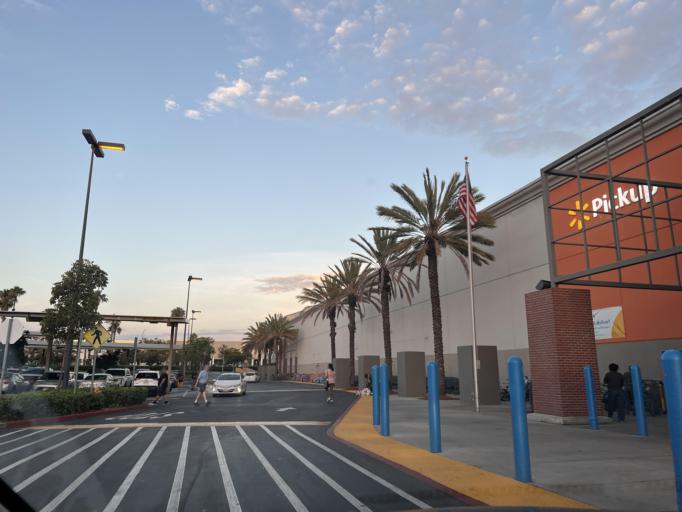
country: US
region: California
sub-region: San Diego County
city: La Jolla
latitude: 32.8301
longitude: -117.1656
